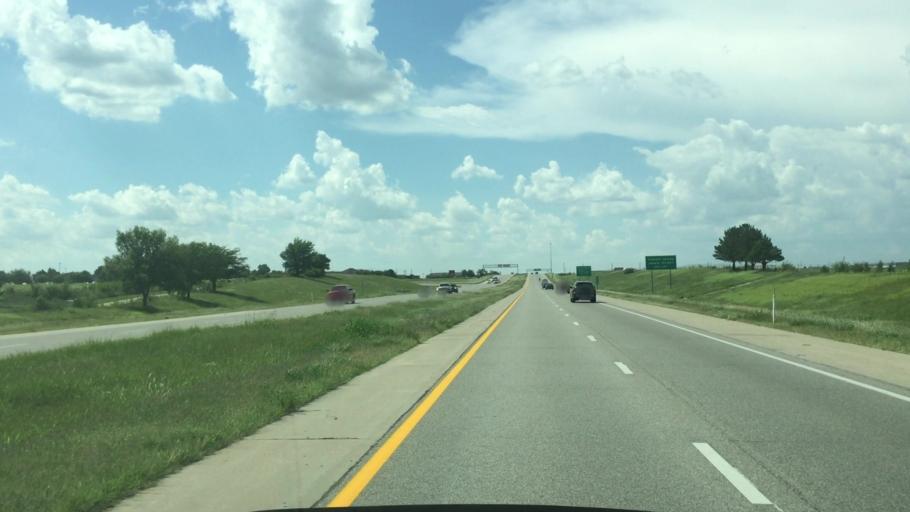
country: US
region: Kansas
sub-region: Sedgwick County
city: Bellaire
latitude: 37.7326
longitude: -97.2197
